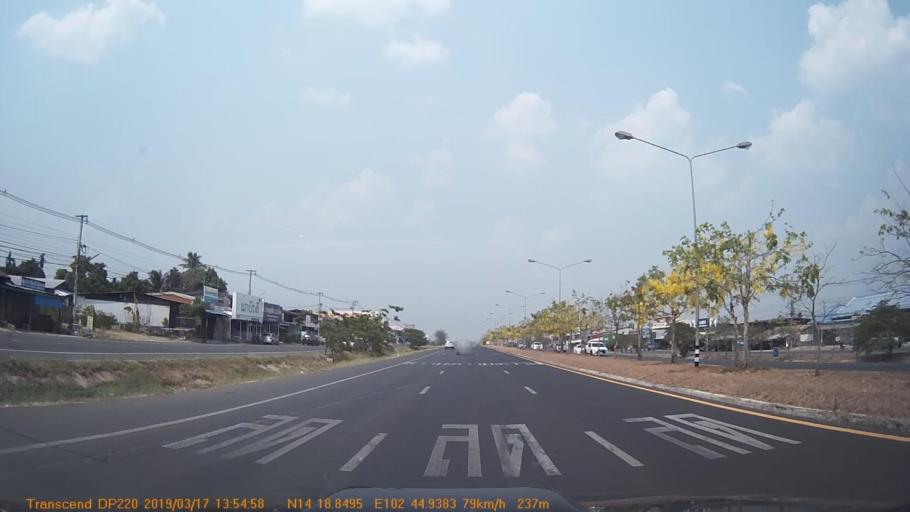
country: TH
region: Buriram
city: Non Din Daeng
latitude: 14.3144
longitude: 102.7491
